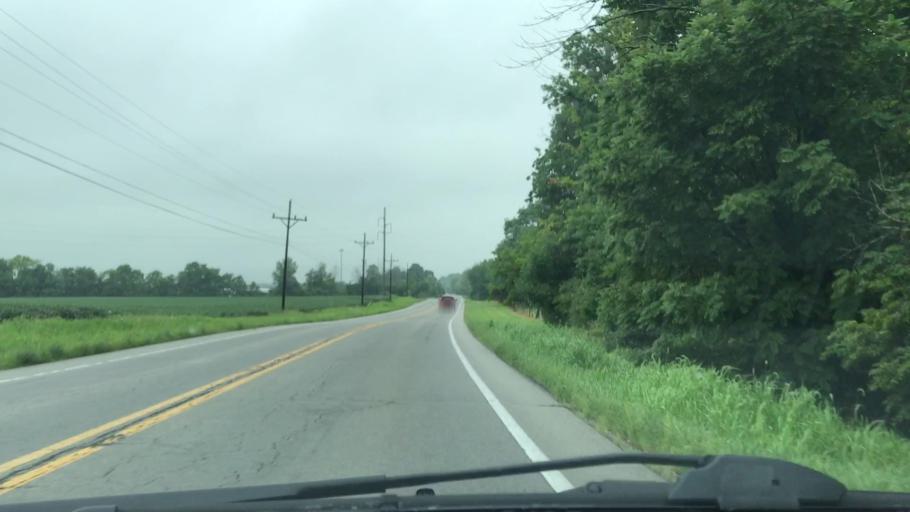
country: US
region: Indiana
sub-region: Hamilton County
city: Westfield
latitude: 40.0791
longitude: -86.0933
